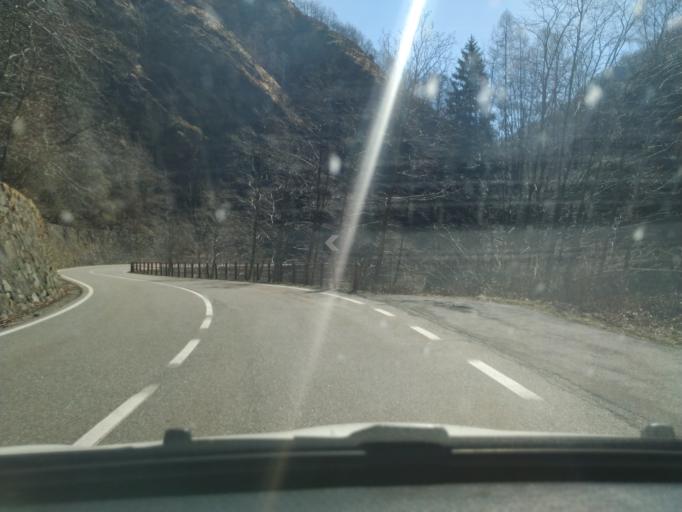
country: IT
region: Piedmont
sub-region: Provincia di Vercelli
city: Cervatto
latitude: 45.8723
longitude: 8.1850
